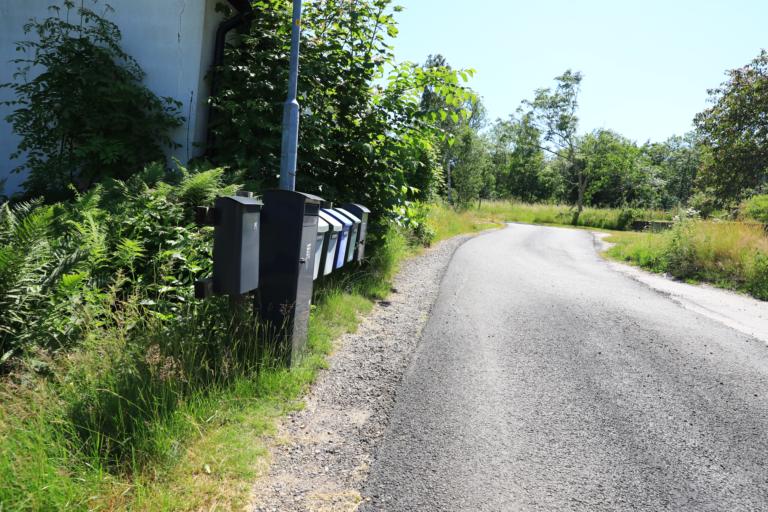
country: SE
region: Halland
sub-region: Varbergs Kommun
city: Varberg
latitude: 57.1743
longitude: 12.2975
